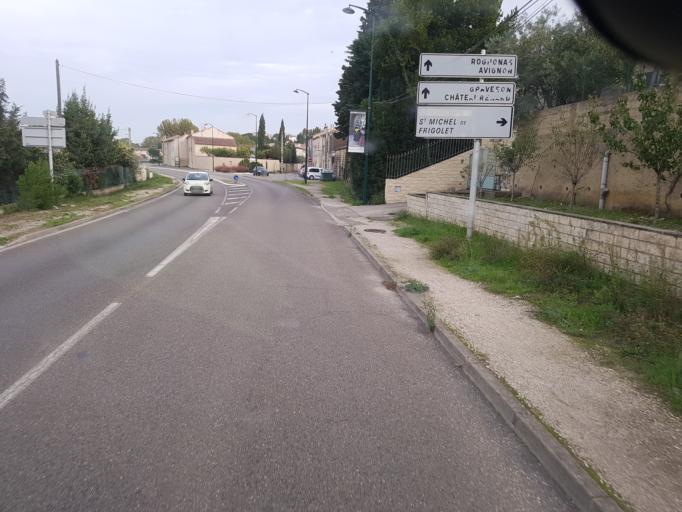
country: FR
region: Provence-Alpes-Cote d'Azur
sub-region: Departement des Bouches-du-Rhone
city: Barbentane
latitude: 43.8991
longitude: 4.7392
